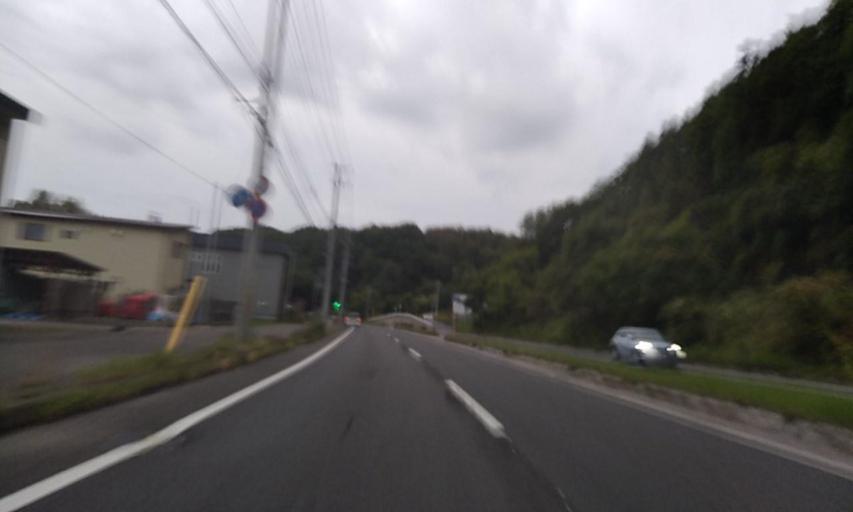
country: JP
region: Hokkaido
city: Abashiri
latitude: 43.9890
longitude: 144.2955
